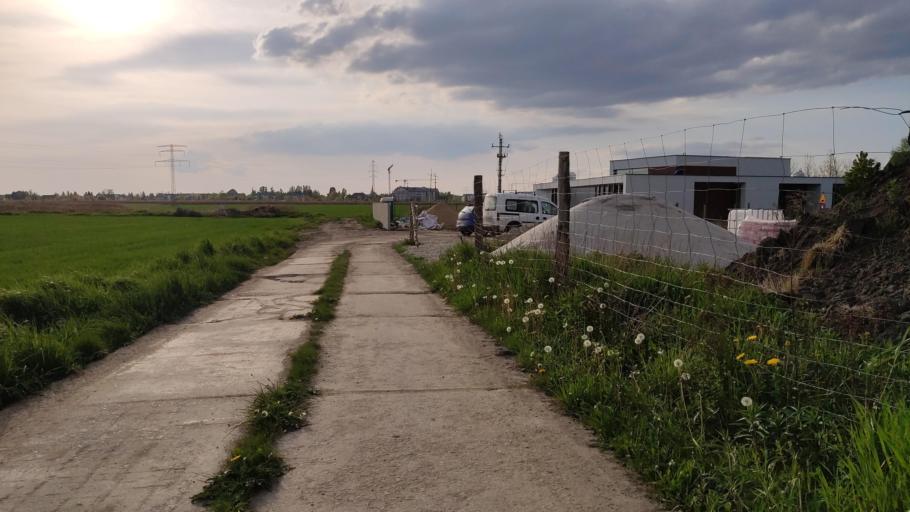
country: PL
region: Lower Silesian Voivodeship
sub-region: Powiat wroclawski
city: Zerniki Wroclawskie
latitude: 51.0497
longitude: 17.0477
